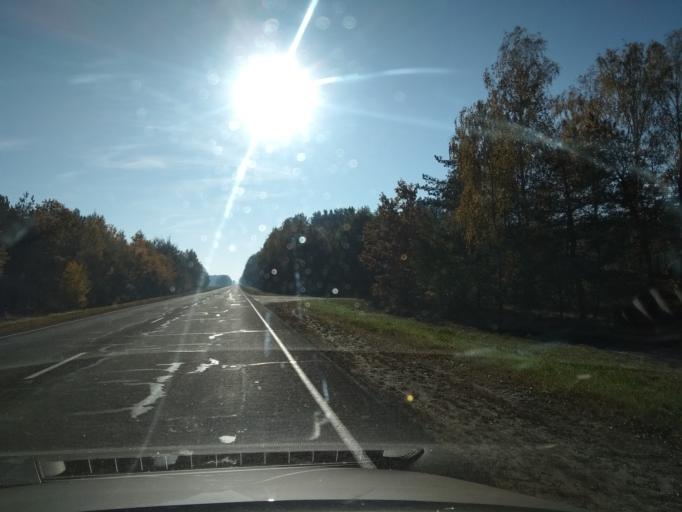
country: BY
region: Brest
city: Malaryta
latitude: 51.8833
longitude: 24.1575
